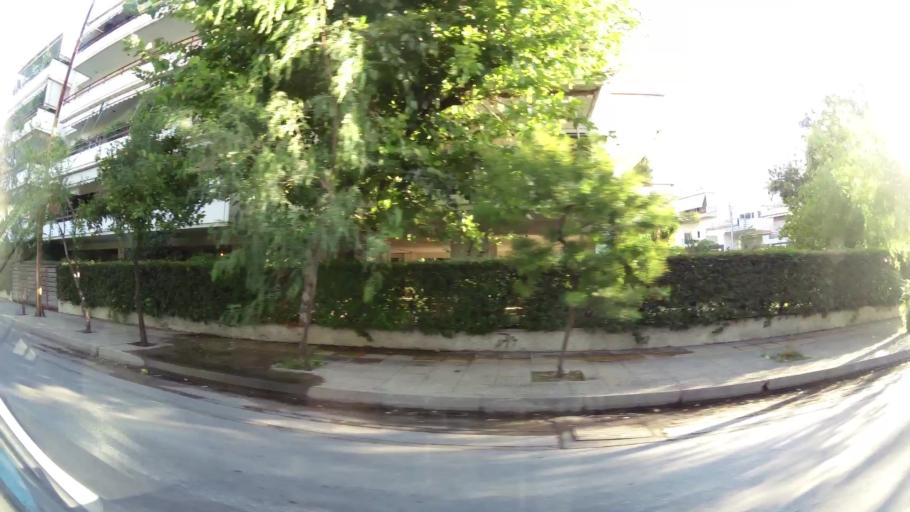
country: GR
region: Attica
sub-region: Nomarchia Athinas
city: Neo Psychiko
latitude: 38.0078
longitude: 23.7871
